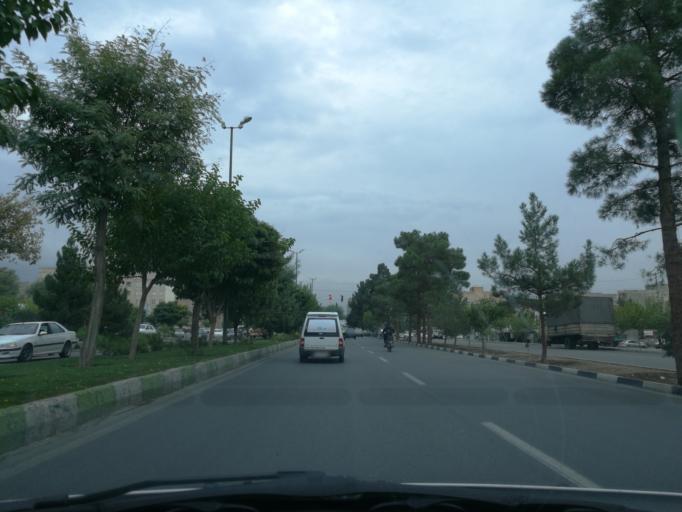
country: IR
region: Alborz
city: Karaj
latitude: 35.8581
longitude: 50.9475
